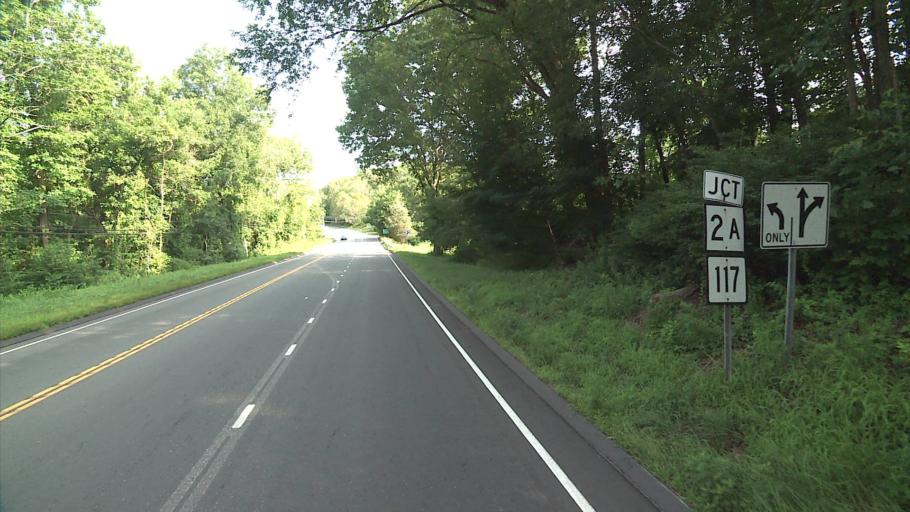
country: US
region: Connecticut
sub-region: New London County
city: Norwich
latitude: 41.4977
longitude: -72.0313
